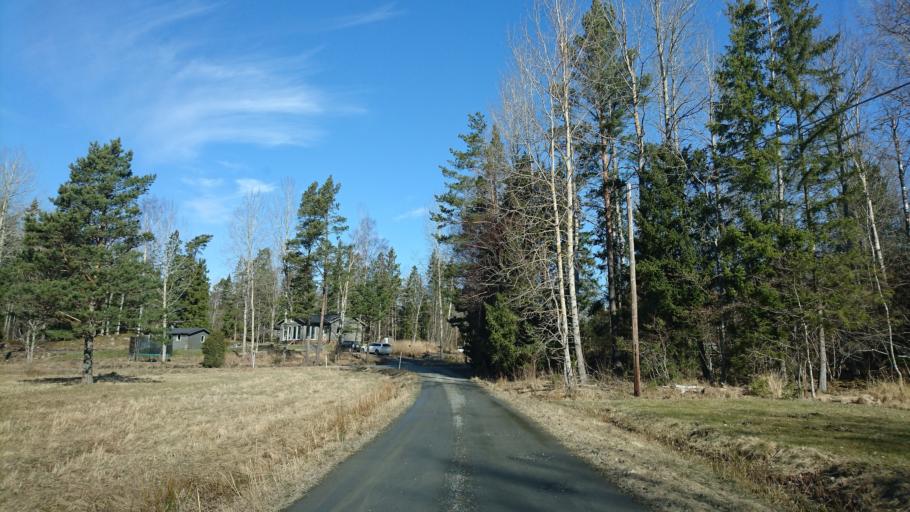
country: SE
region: Stockholm
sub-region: Norrtalje Kommun
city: Bjorko
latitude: 59.7920
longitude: 18.9954
